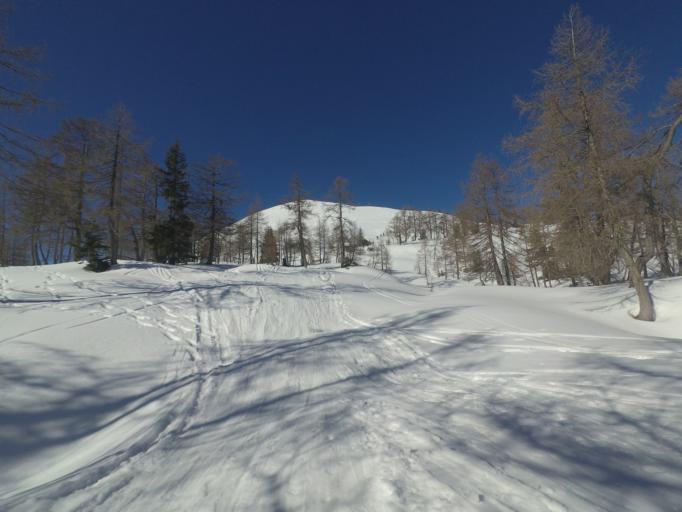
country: AT
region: Upper Austria
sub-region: Politischer Bezirk Gmunden
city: Sankt Wolfgang im Salzkammergut
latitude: 47.6652
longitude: 13.3807
